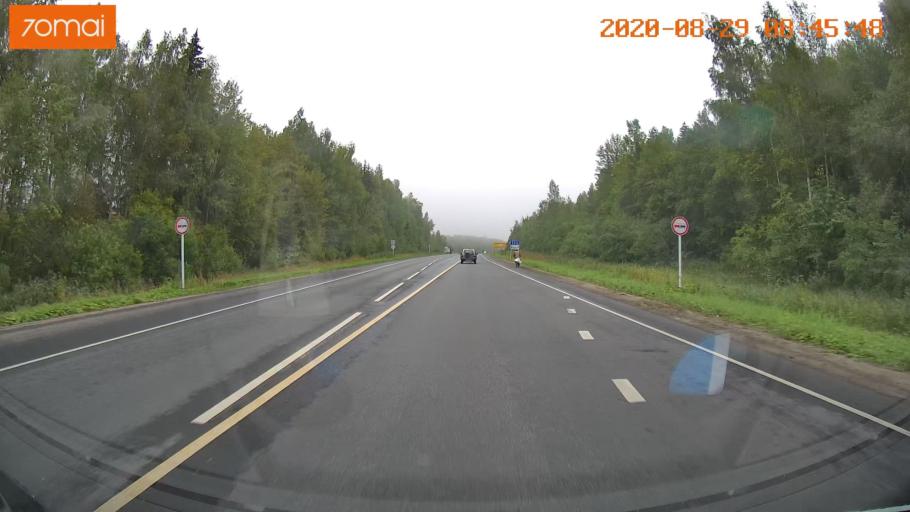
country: RU
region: Ivanovo
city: Rodniki
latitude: 57.1350
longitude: 41.8052
